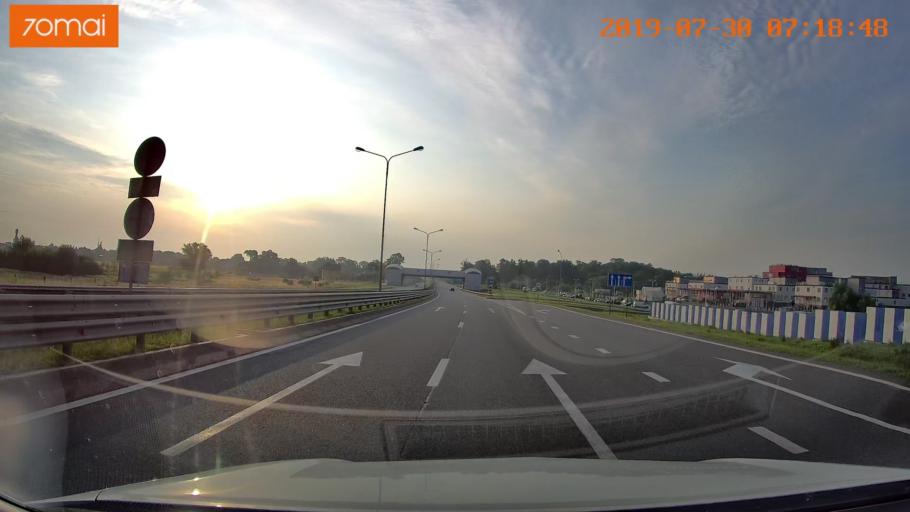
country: RU
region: Kaliningrad
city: Bol'shoe Isakovo
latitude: 54.7025
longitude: 20.6573
